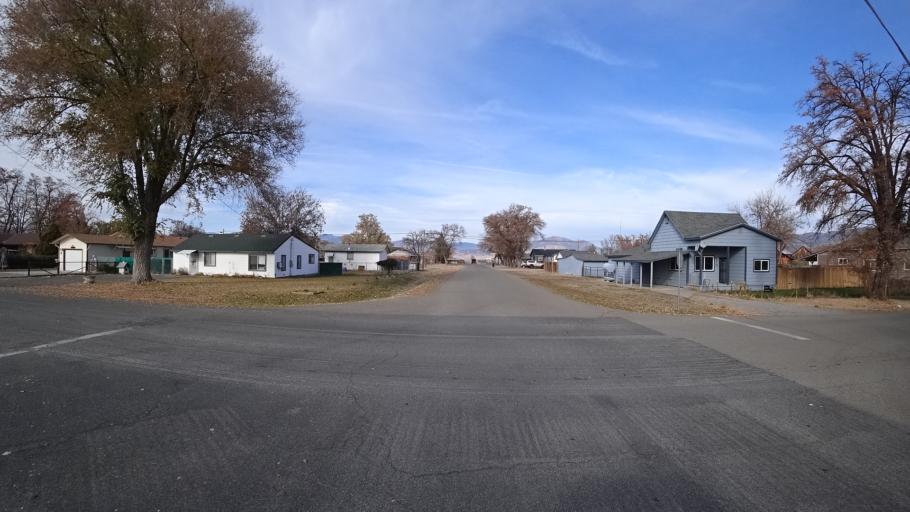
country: US
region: California
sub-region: Siskiyou County
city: Montague
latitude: 41.7285
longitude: -122.5323
